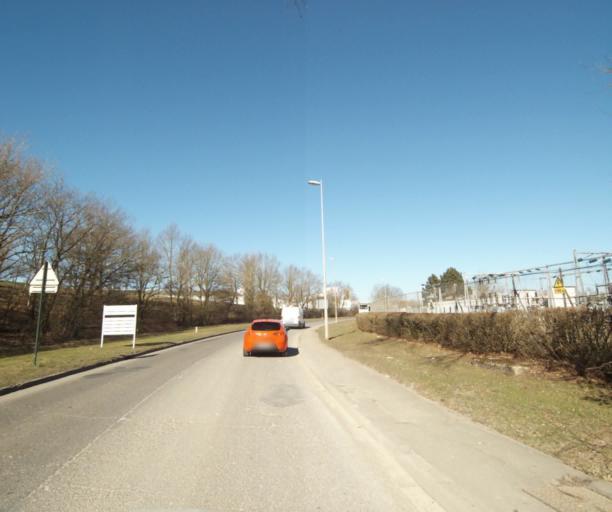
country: FR
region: Lorraine
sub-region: Departement de Meurthe-et-Moselle
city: Fleville-devant-Nancy
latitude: 48.6108
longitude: 6.1911
